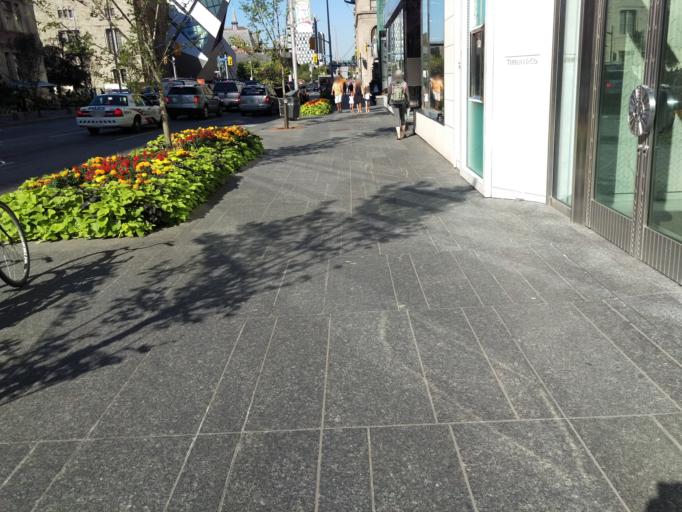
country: CA
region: Ontario
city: Toronto
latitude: 43.6689
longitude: -79.3935
